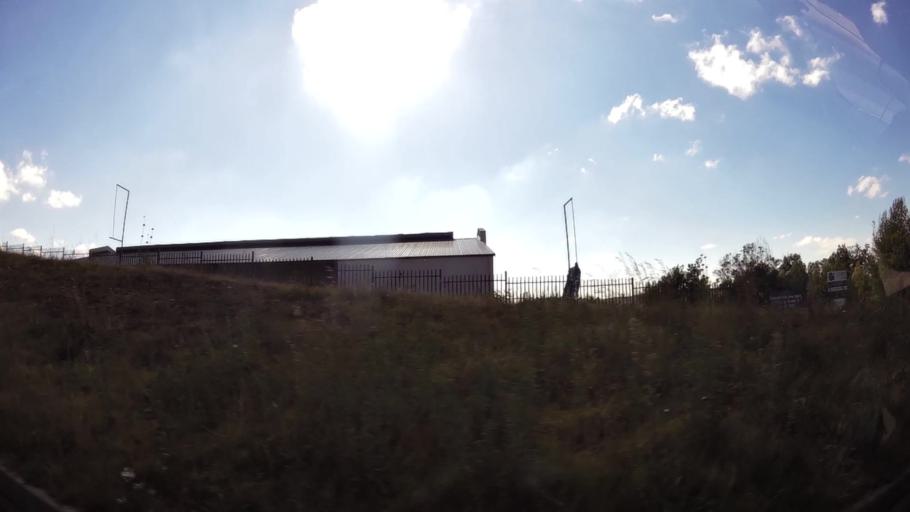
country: ZA
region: Gauteng
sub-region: West Rand District Municipality
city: Krugersdorp
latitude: -26.0856
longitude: 27.8086
